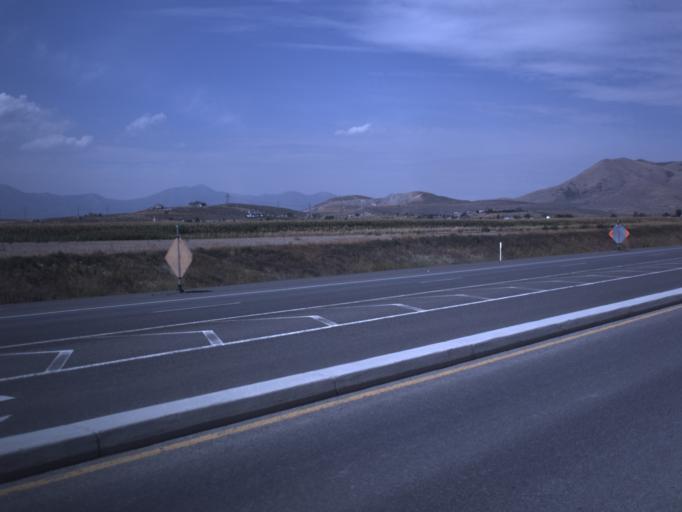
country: US
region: Utah
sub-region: Utah County
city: Saratoga Springs
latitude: 40.3771
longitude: -111.9244
